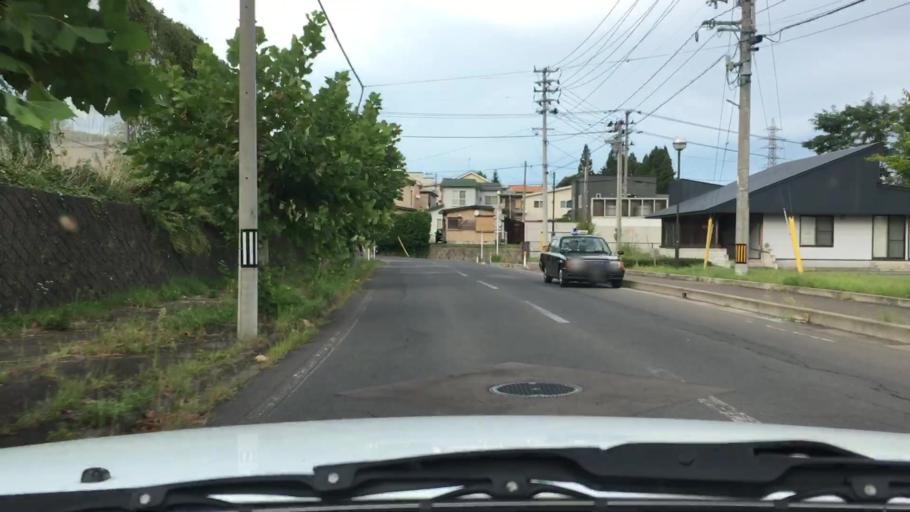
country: JP
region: Aomori
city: Hirosaki
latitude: 40.5773
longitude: 140.4566
